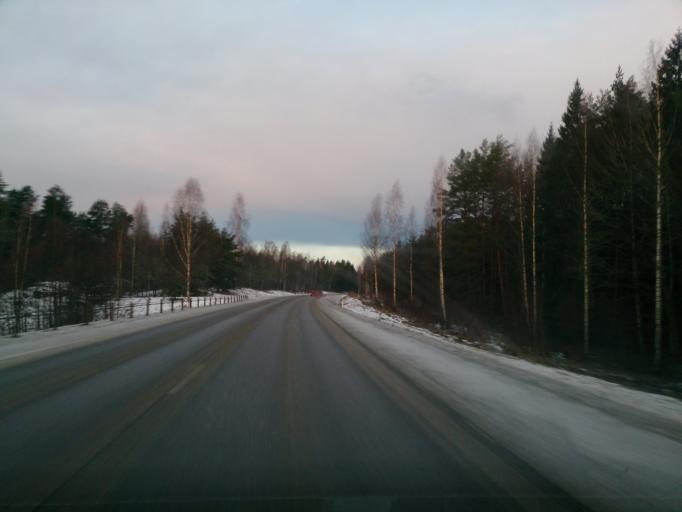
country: SE
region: OEstergoetland
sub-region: Atvidabergs Kommun
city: Atvidaberg
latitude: 58.2368
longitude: 15.9458
